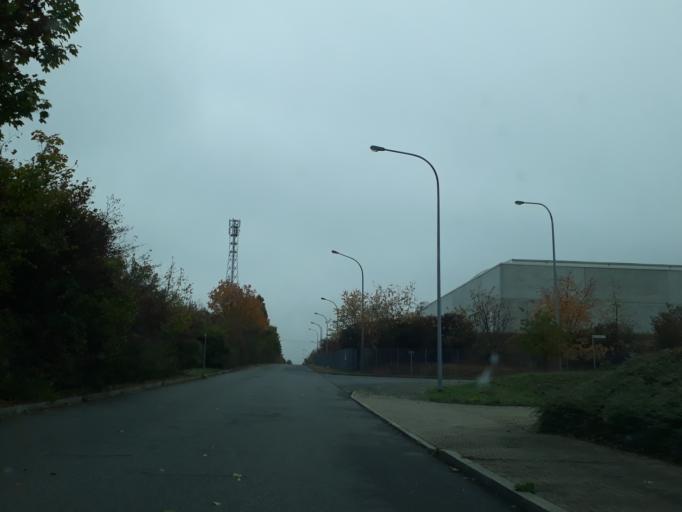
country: DE
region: Saxony
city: Radeburg
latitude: 51.2035
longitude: 13.7326
